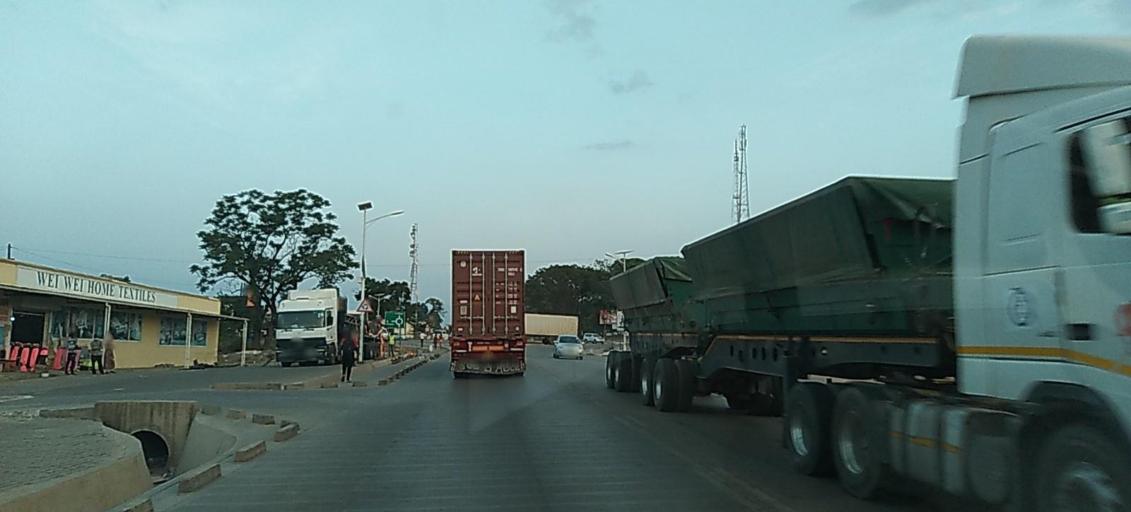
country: ZM
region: Copperbelt
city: Chingola
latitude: -12.5476
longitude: 27.8564
